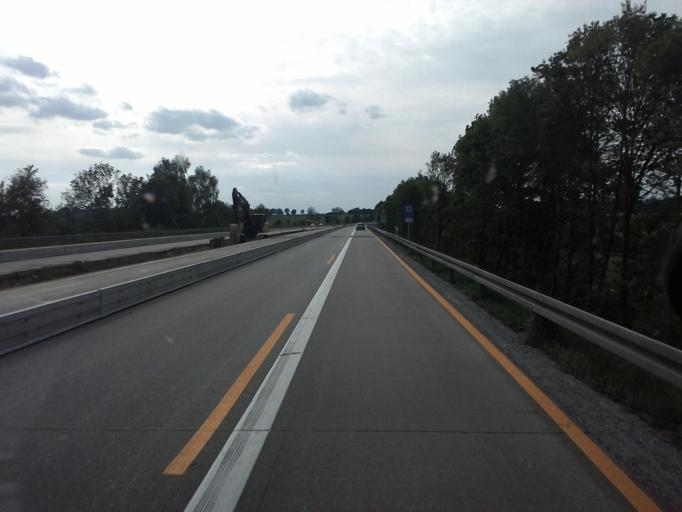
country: DE
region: Bavaria
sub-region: Lower Bavaria
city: Windberg
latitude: 48.9221
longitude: 12.7299
